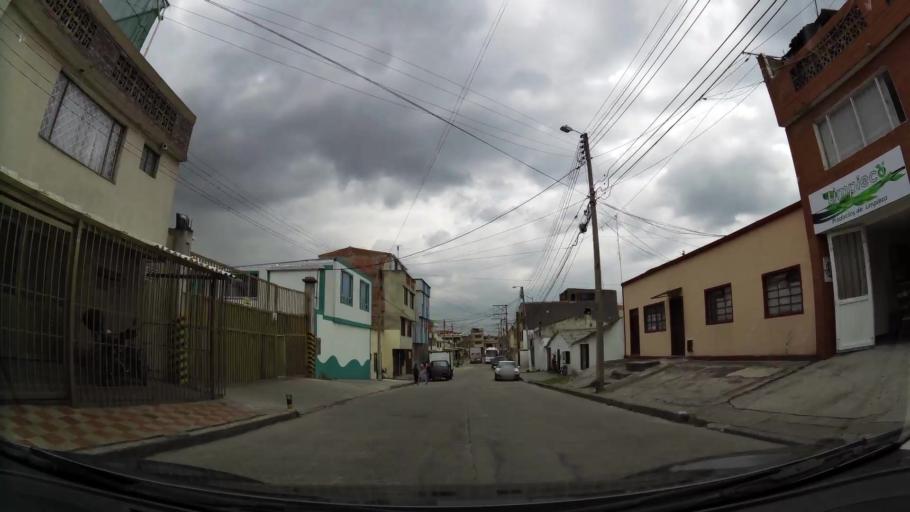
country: CO
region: Cundinamarca
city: La Calera
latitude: 4.7581
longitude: -74.0293
